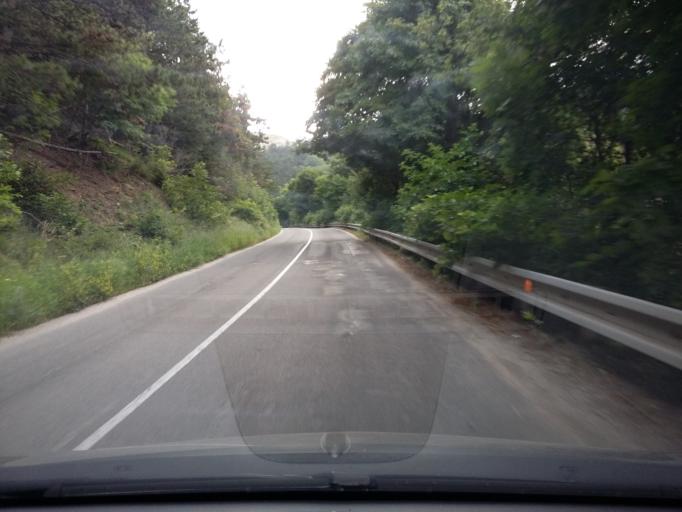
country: SK
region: Trnavsky
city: Smolenice
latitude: 48.5430
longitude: 17.4181
